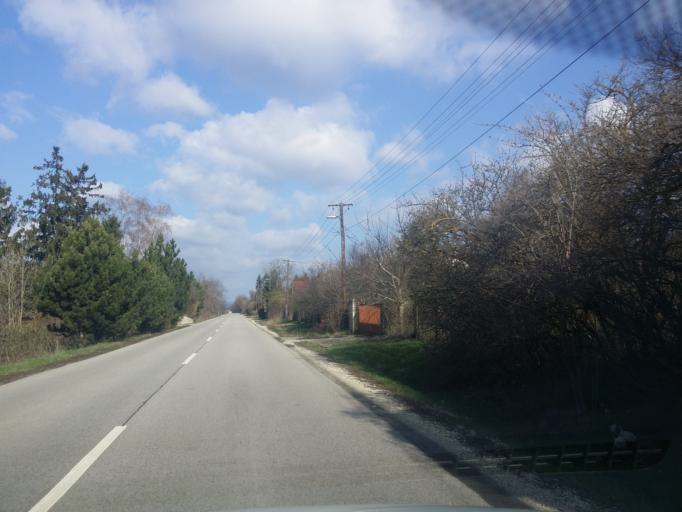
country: HU
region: Pest
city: Zsambek
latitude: 47.5708
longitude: 18.6836
